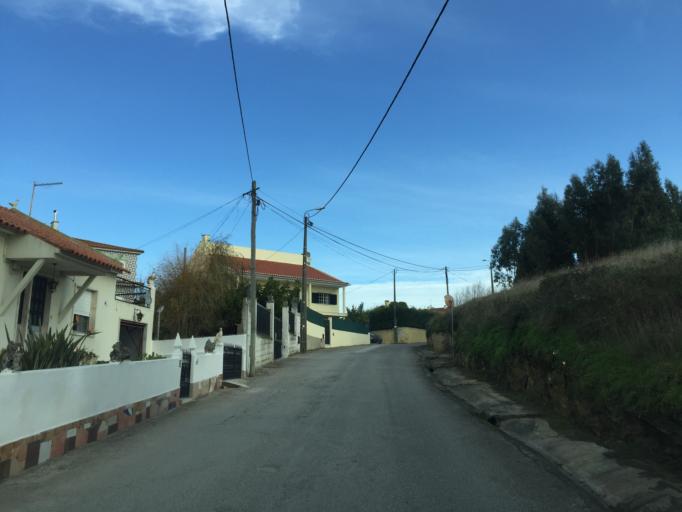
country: PT
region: Lisbon
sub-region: Odivelas
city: Canecas
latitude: 38.8174
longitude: -9.2488
